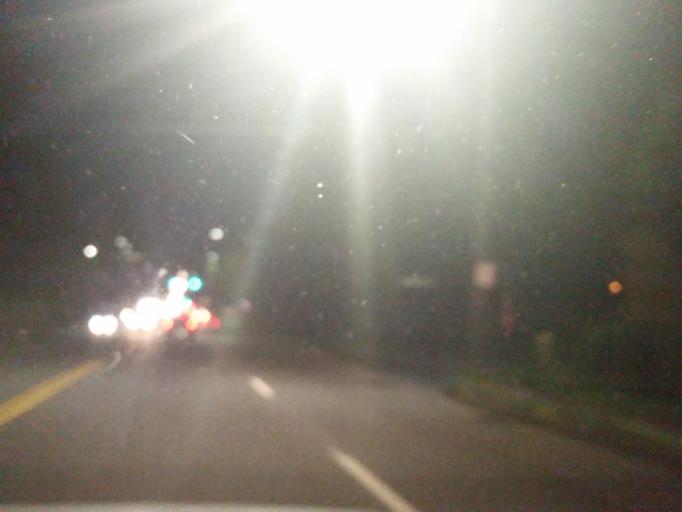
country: US
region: Washington
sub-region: King County
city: Shoreline
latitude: 47.7342
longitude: -122.3305
